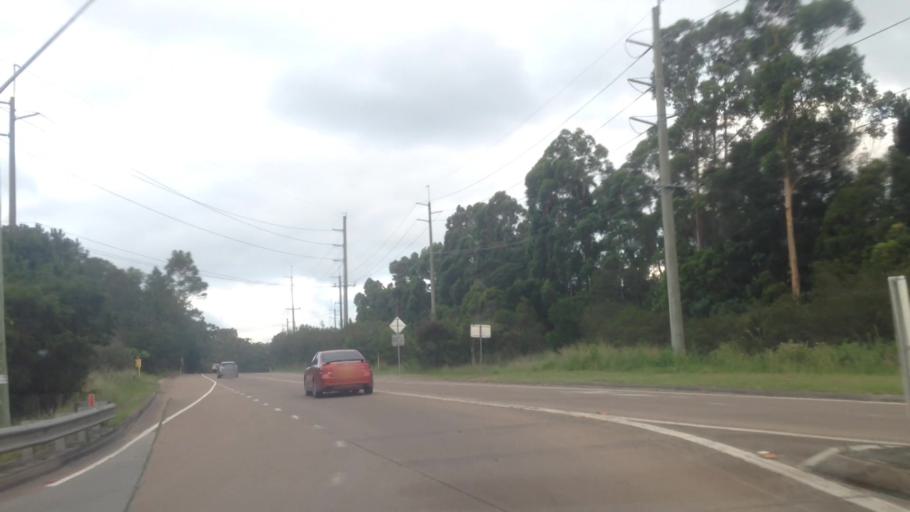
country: AU
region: New South Wales
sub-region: Lake Macquarie Shire
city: Cooranbong
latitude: -33.1158
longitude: 151.4704
